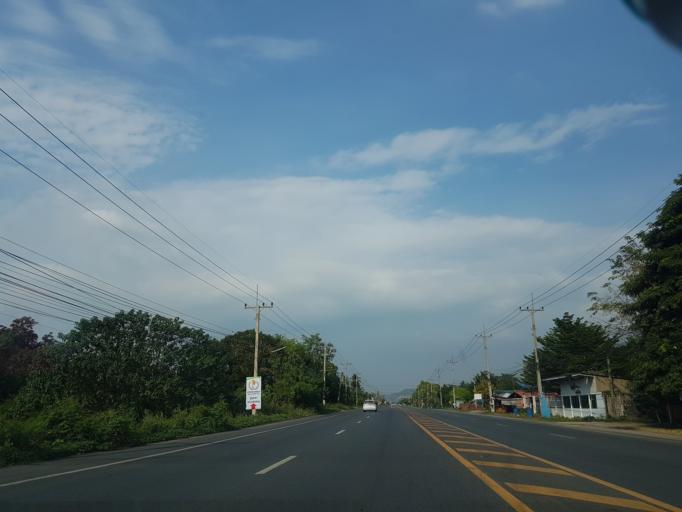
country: TH
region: Sara Buri
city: Ban Mo
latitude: 14.6379
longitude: 100.7547
